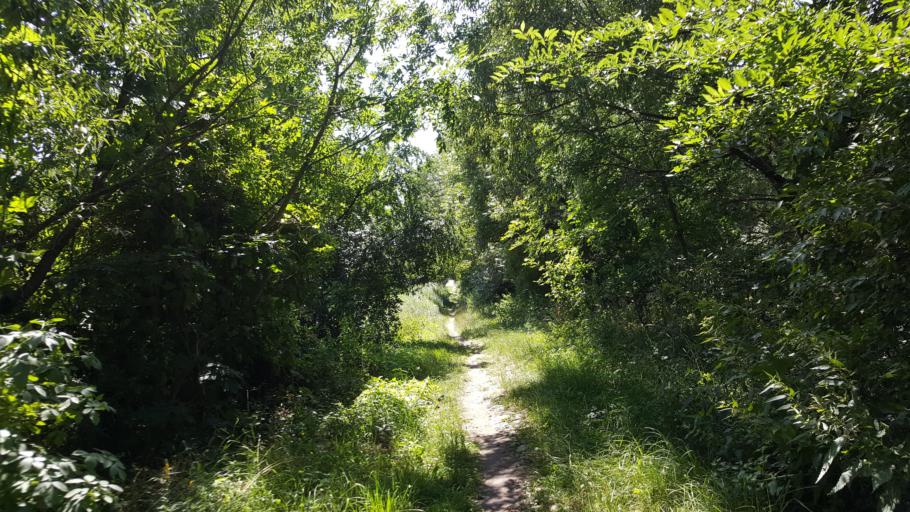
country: BY
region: Brest
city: Vysokaye
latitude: 52.3738
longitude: 23.3735
